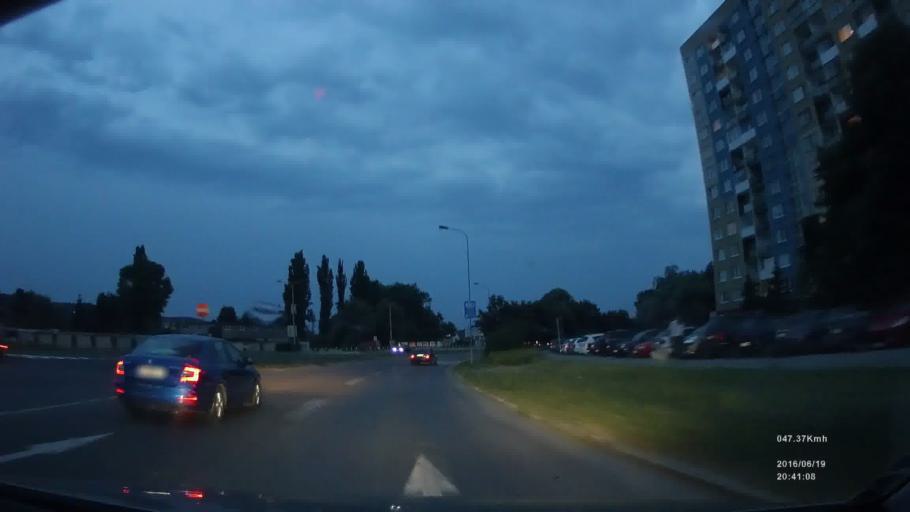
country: SK
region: Kosicky
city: Kosice
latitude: 48.7164
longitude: 21.2668
